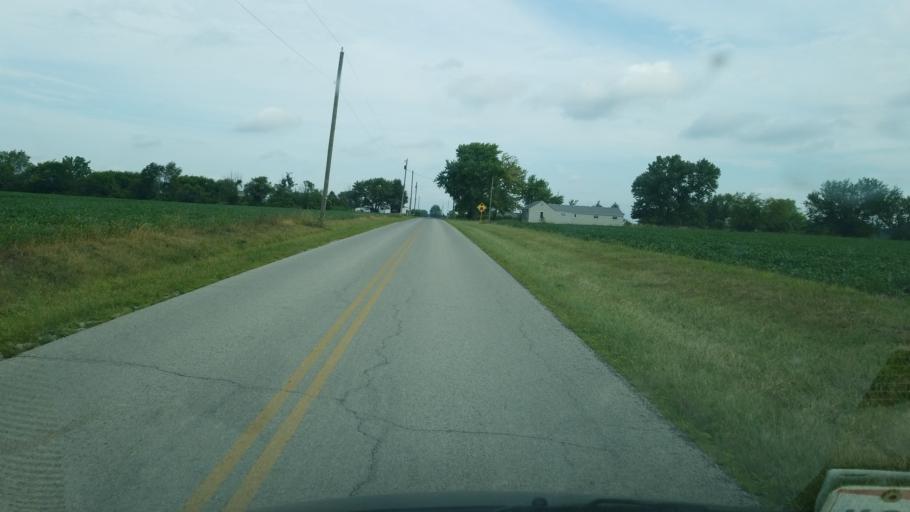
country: US
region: Ohio
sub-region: Seneca County
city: Tiffin
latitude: 41.0924
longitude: -83.0930
